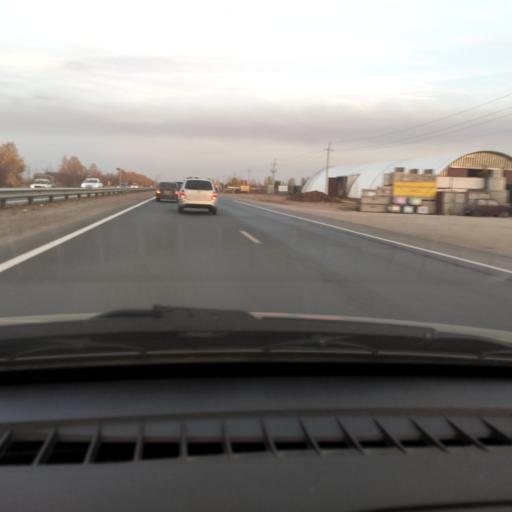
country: RU
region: Samara
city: Tol'yatti
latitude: 53.5782
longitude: 49.4160
